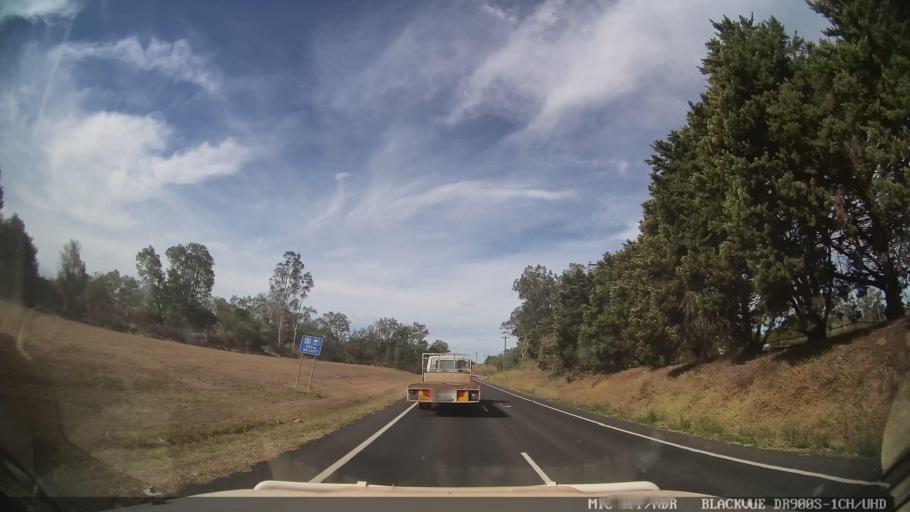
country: AU
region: Queensland
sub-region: Tablelands
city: Mareeba
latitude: -17.0073
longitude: 145.4370
